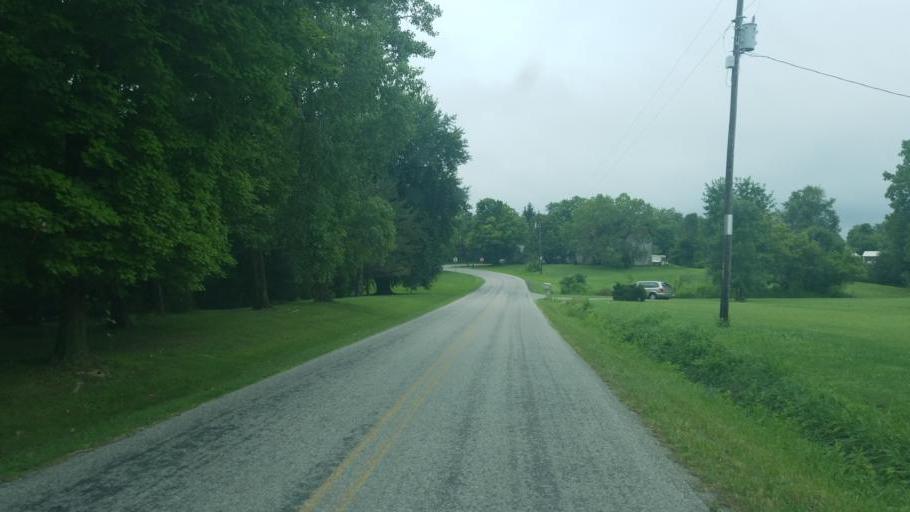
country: US
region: Ohio
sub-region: Delaware County
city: Sunbury
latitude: 40.3282
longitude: -82.8169
